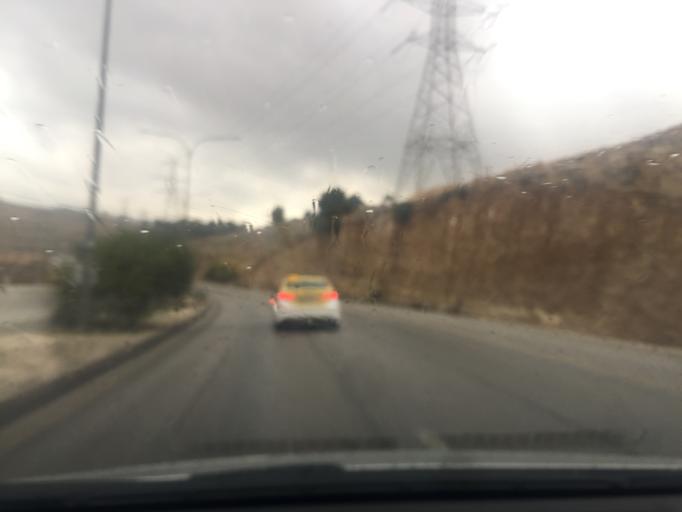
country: JO
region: Amman
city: Amman
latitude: 32.0248
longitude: 35.9675
